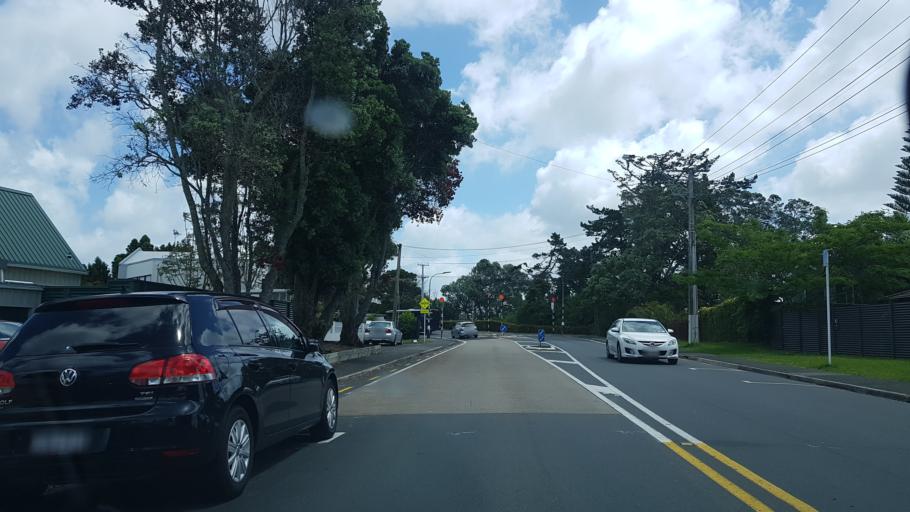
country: NZ
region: Auckland
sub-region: Auckland
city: North Shore
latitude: -36.8077
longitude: 174.6989
